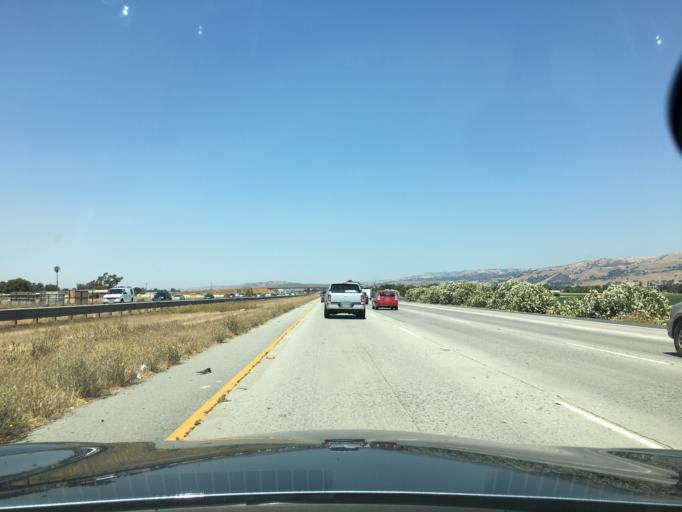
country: US
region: California
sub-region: Santa Clara County
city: San Martin
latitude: 37.0666
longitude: -121.5876
